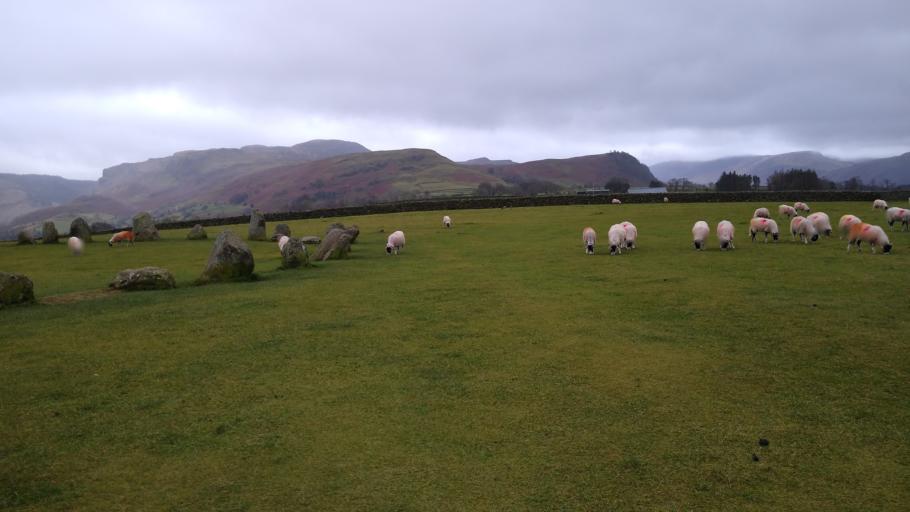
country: GB
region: England
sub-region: Cumbria
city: Keswick
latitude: 54.6031
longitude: -3.0986
